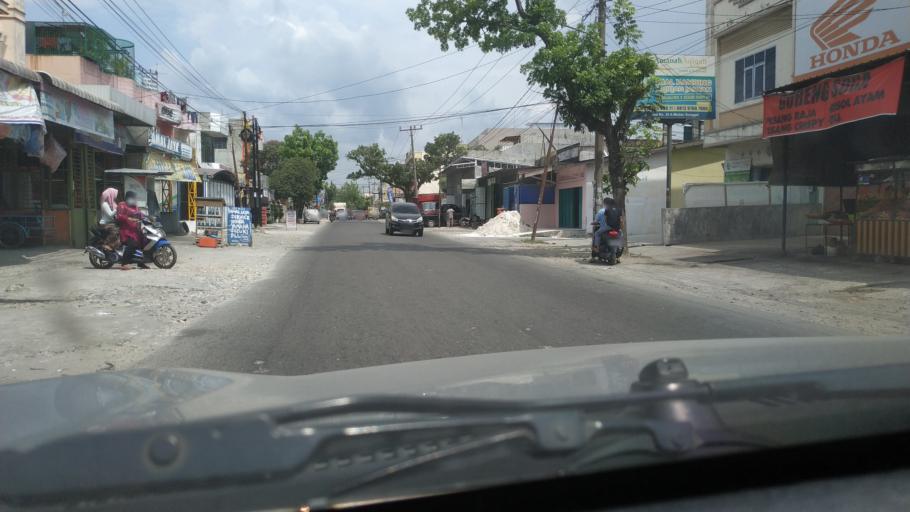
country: ID
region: North Sumatra
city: Sunggal
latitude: 3.5854
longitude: 98.6160
